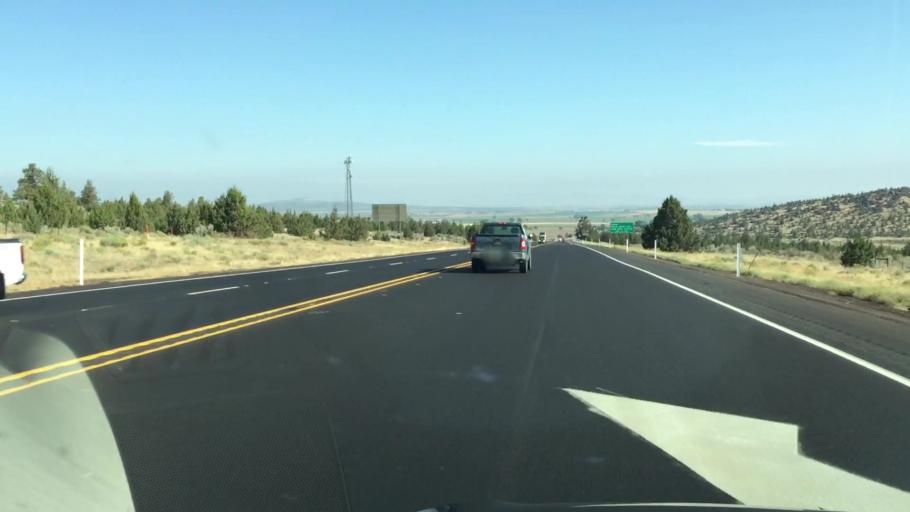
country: US
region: Oregon
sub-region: Jefferson County
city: Culver
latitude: 44.4826
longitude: -121.1933
